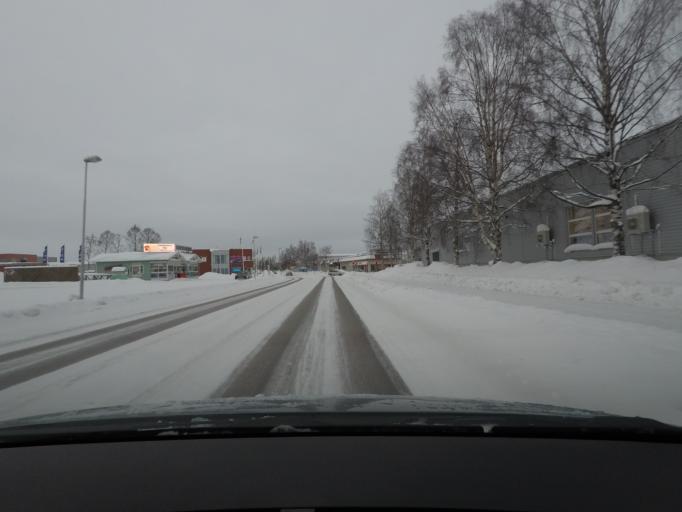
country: SE
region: Norrbotten
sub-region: Lulea Kommun
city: Lulea
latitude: 65.5986
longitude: 22.1445
